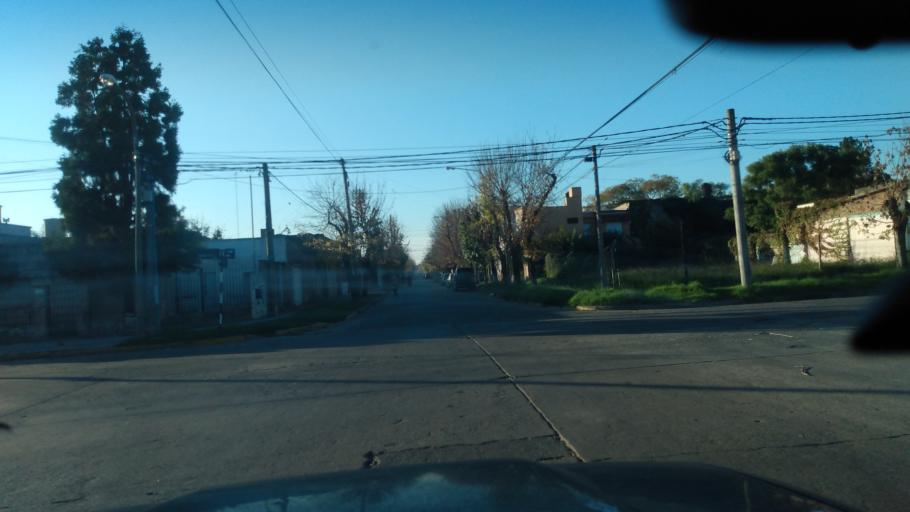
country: AR
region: Buenos Aires
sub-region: Partido de Lujan
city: Lujan
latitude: -34.5622
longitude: -59.1088
